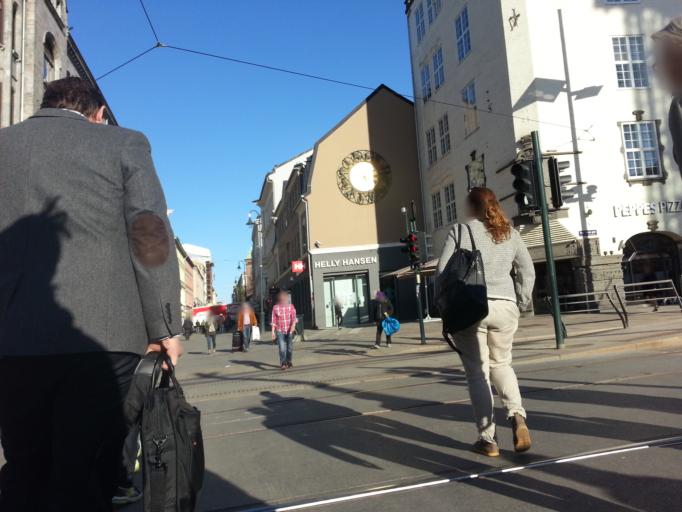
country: NO
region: Oslo
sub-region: Oslo
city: Oslo
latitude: 59.9112
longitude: 10.7498
